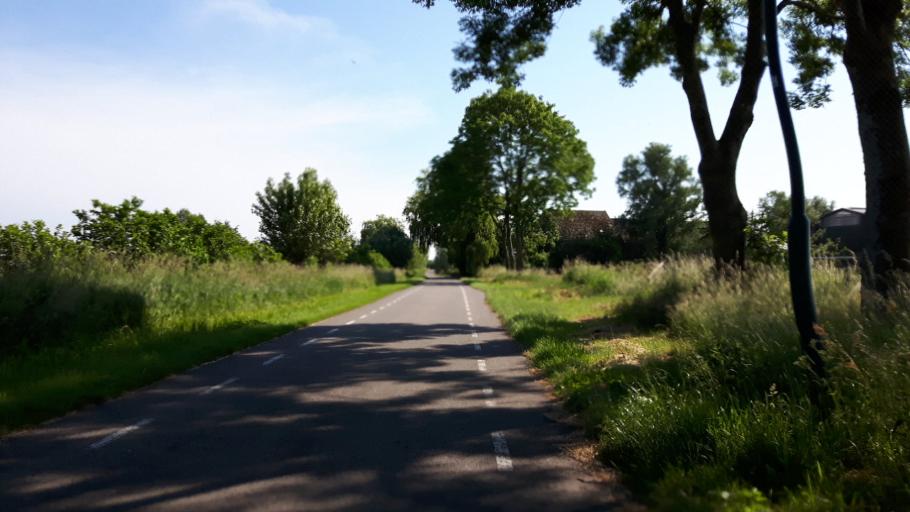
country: NL
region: Utrecht
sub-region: Stichtse Vecht
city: Breukelen
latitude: 52.2148
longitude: 4.9807
